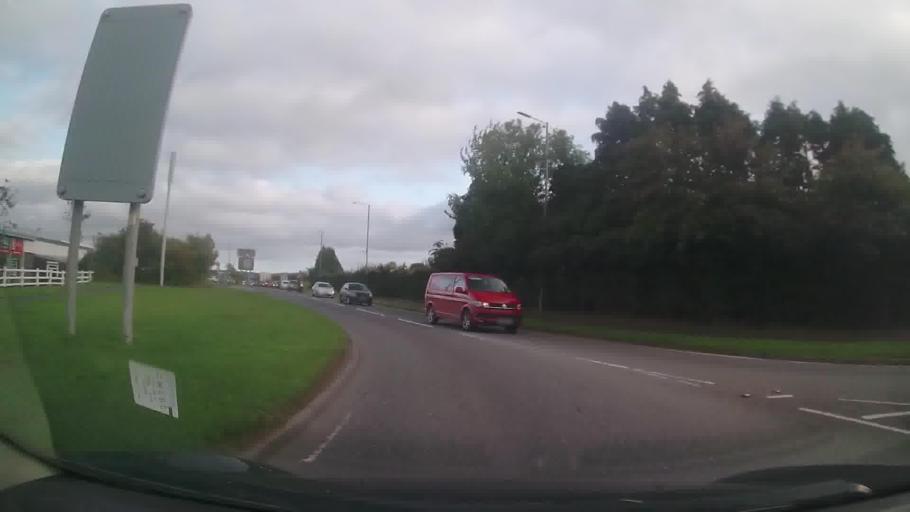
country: GB
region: Wales
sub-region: Pembrokeshire
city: Neyland
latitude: 51.7181
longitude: -4.9552
